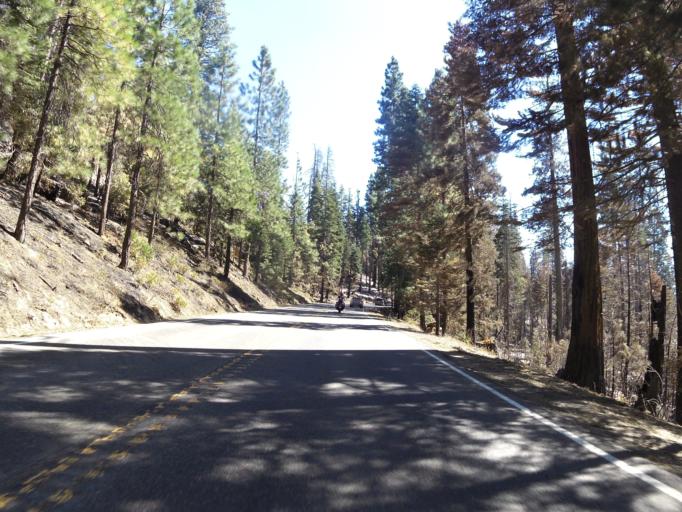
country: US
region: California
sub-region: Mariposa County
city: Yosemite Valley
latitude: 37.6807
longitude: -119.7080
